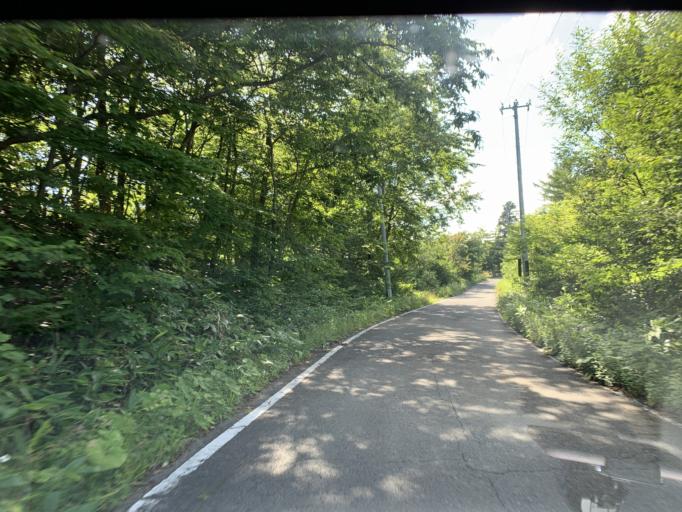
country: JP
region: Iwate
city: Ichinoseki
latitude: 38.9025
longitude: 140.8682
